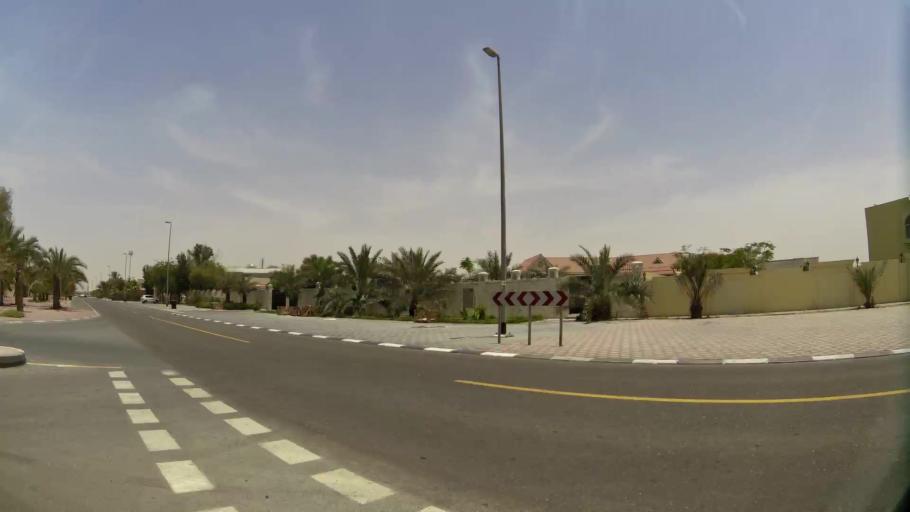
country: AE
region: Ash Shariqah
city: Sharjah
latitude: 25.2396
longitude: 55.4540
